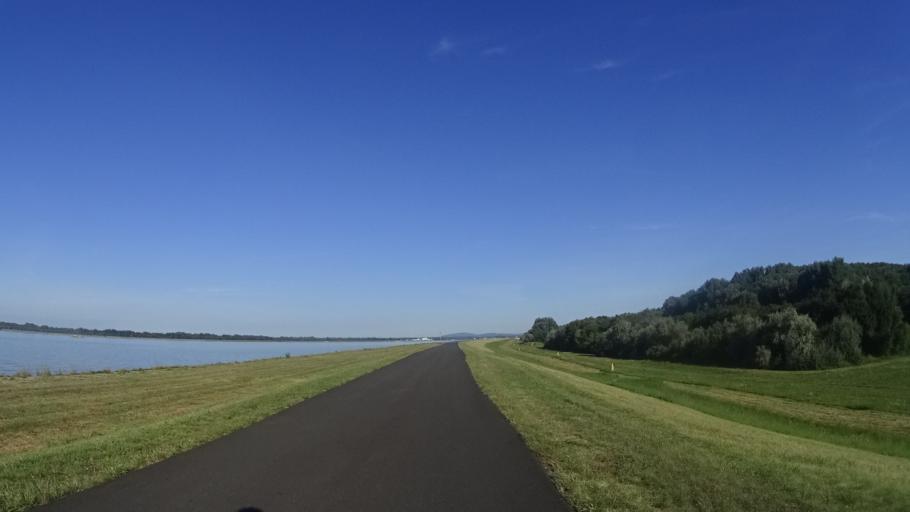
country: SK
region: Trnavsky
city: Samorin
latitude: 48.0254
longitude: 17.2676
